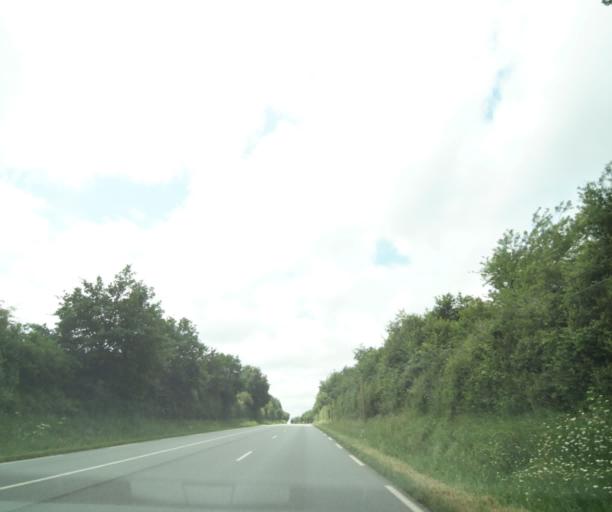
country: FR
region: Poitou-Charentes
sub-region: Departement des Deux-Sevres
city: Le Tallud
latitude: 46.6263
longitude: -0.2769
